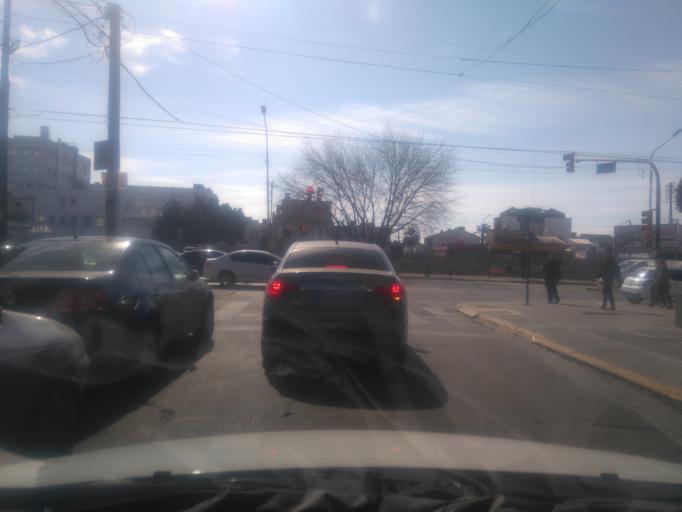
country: AR
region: Buenos Aires
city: San Justo
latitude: -34.6402
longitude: -58.5543
